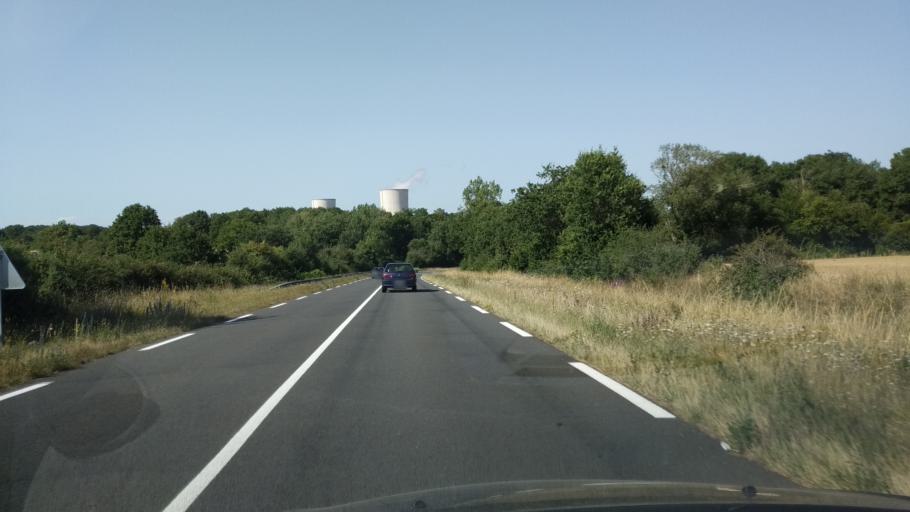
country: FR
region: Poitou-Charentes
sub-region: Departement de la Vienne
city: Lussac-les-Chateaux
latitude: 46.4347
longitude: 0.6488
